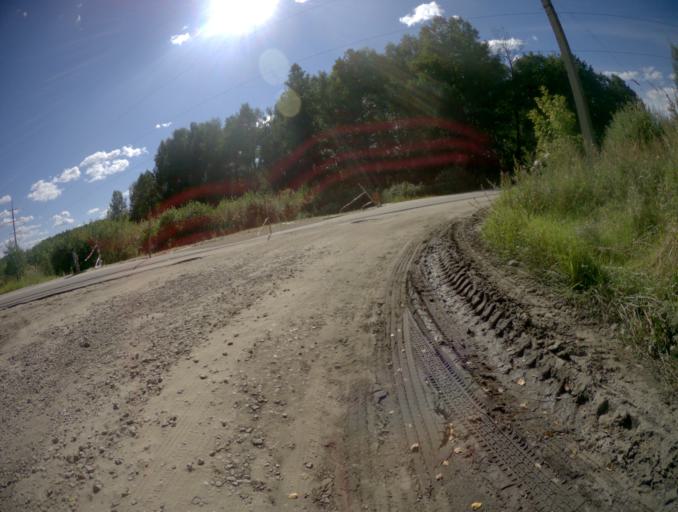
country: RU
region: Vladimir
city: Krasnaya Gorbatka
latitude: 55.8602
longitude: 41.7829
